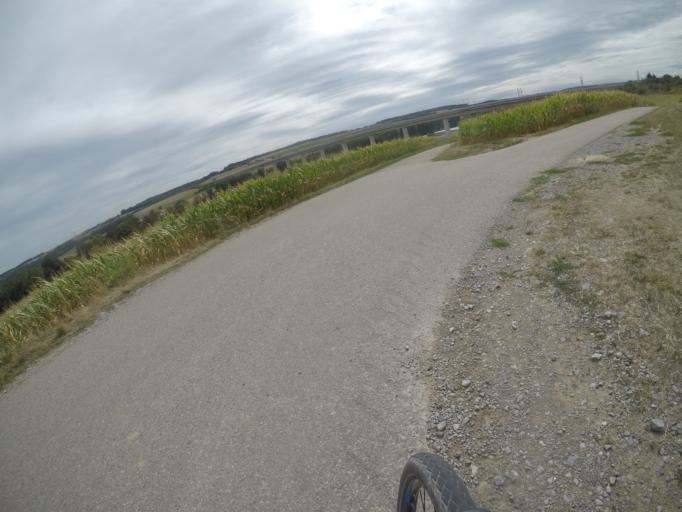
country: DE
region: Baden-Wuerttemberg
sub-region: Regierungsbezirk Stuttgart
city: Oberriexingen
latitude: 48.9282
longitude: 8.9978
